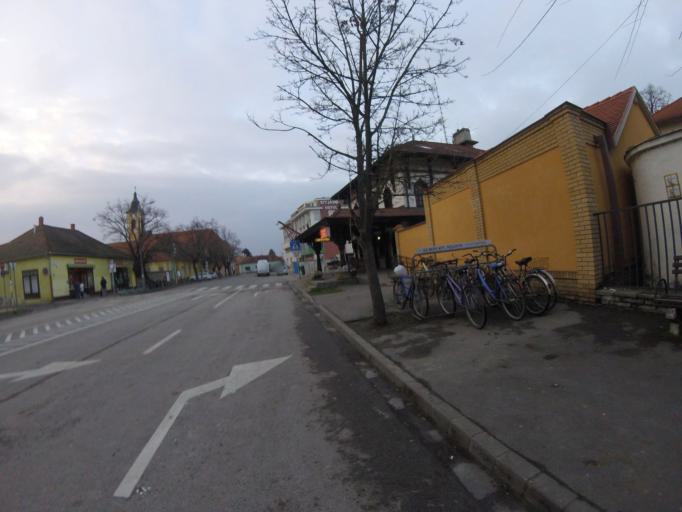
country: HU
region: Baranya
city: Mohacs
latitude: 45.9926
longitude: 18.6940
